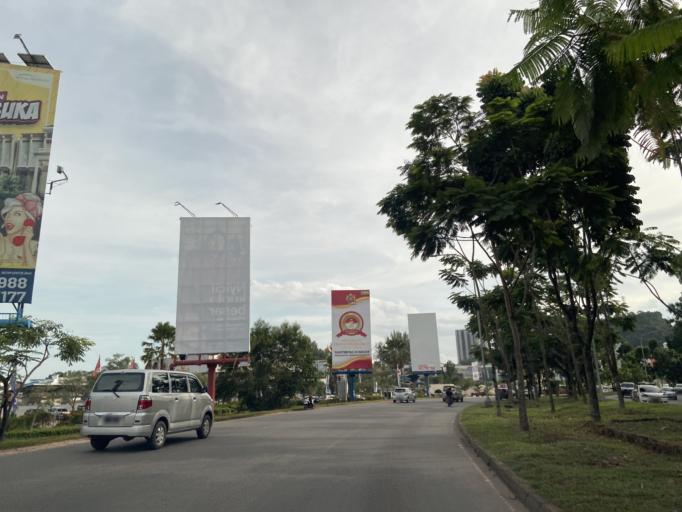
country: SG
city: Singapore
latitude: 1.1293
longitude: 104.0166
